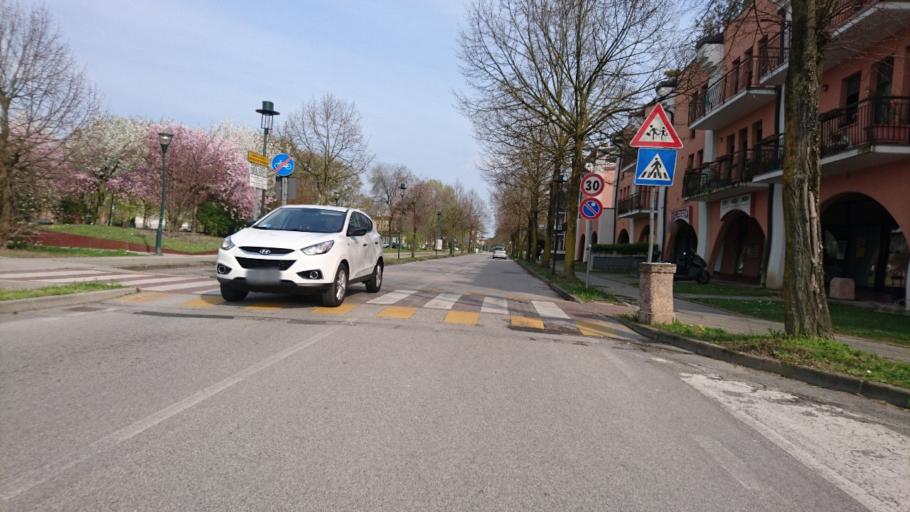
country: IT
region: Veneto
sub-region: Provincia di Padova
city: San Vito
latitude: 45.4291
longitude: 11.9605
